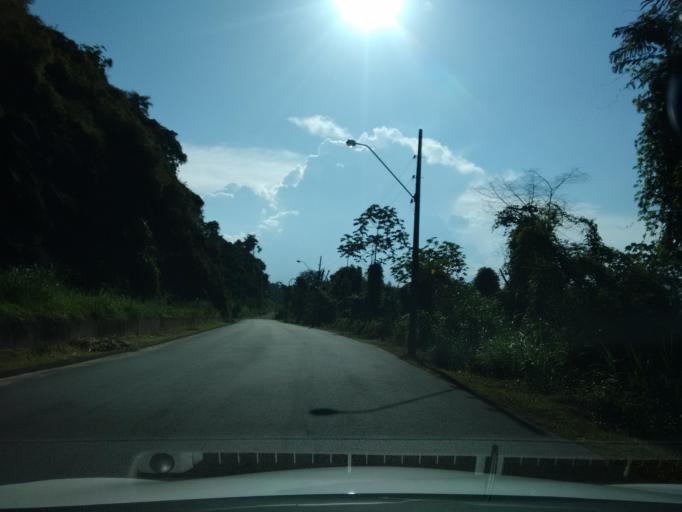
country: BR
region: Santa Catarina
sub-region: Blumenau
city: Blumenau
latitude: -26.8974
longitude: -49.0675
